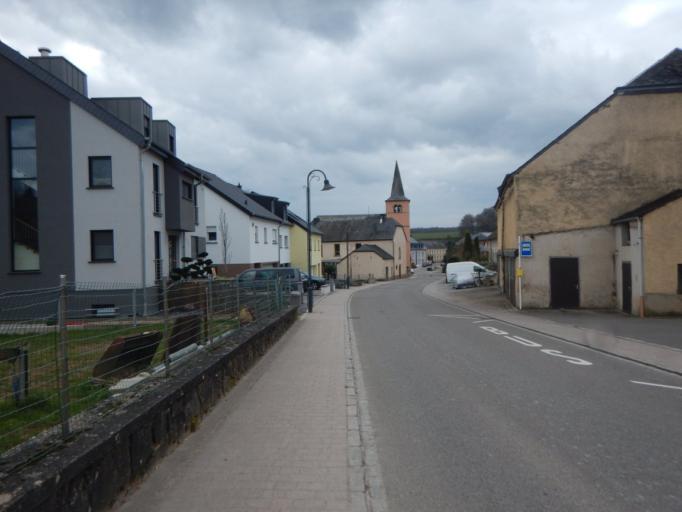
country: LU
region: Diekirch
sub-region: Canton de Redange
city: Ell
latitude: 49.7892
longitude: 5.8579
